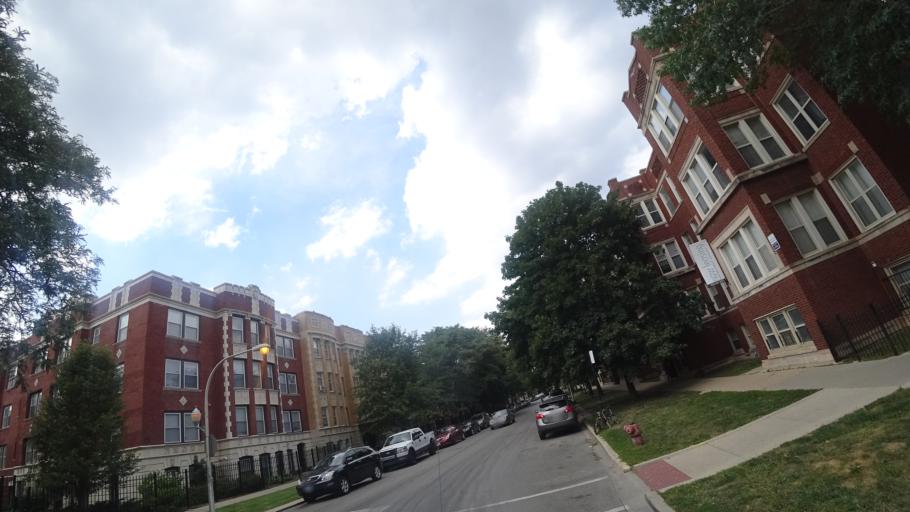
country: US
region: Illinois
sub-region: Cook County
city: Chicago
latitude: 41.7994
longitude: -87.6039
